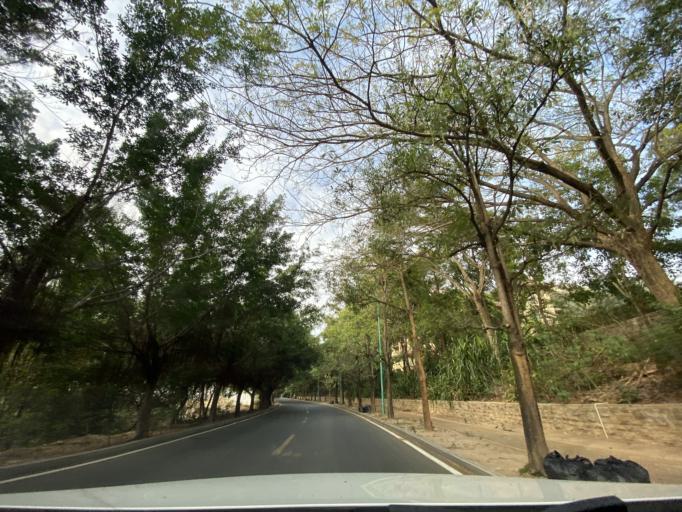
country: CN
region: Hainan
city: Tiandu
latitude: 18.2239
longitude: 109.6203
